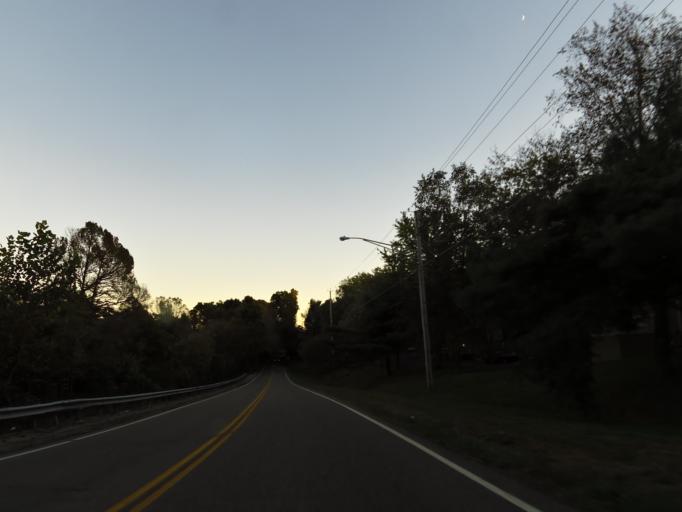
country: US
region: Tennessee
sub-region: Knox County
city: Knoxville
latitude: 36.0199
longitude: -83.9767
